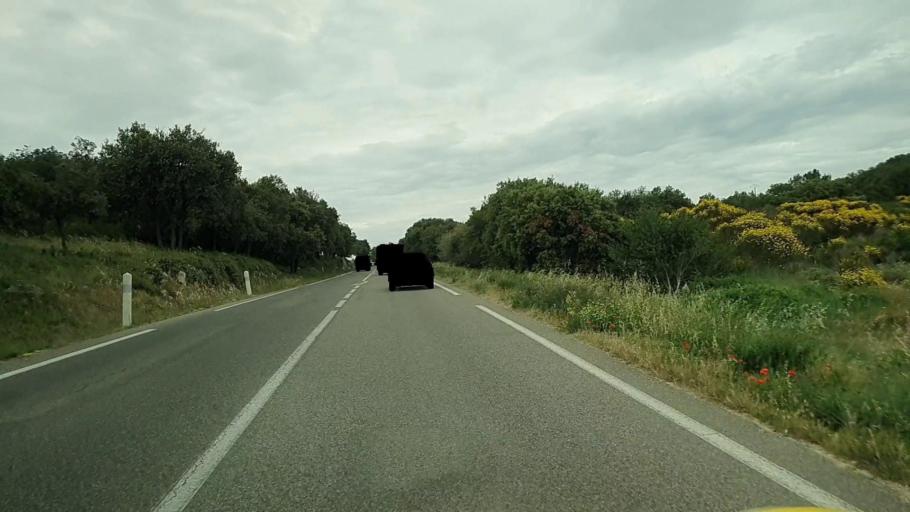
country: FR
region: Languedoc-Roussillon
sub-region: Departement du Gard
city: Connaux
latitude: 44.0319
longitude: 4.5812
